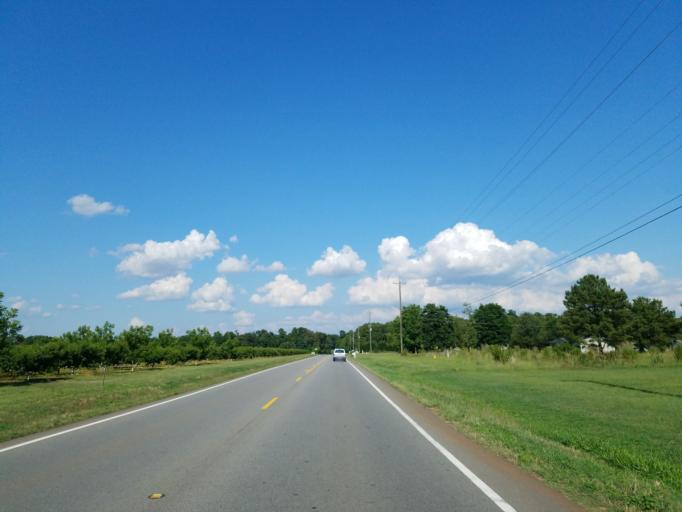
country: US
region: Georgia
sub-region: Peach County
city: Fort Valley
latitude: 32.5567
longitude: -83.8447
